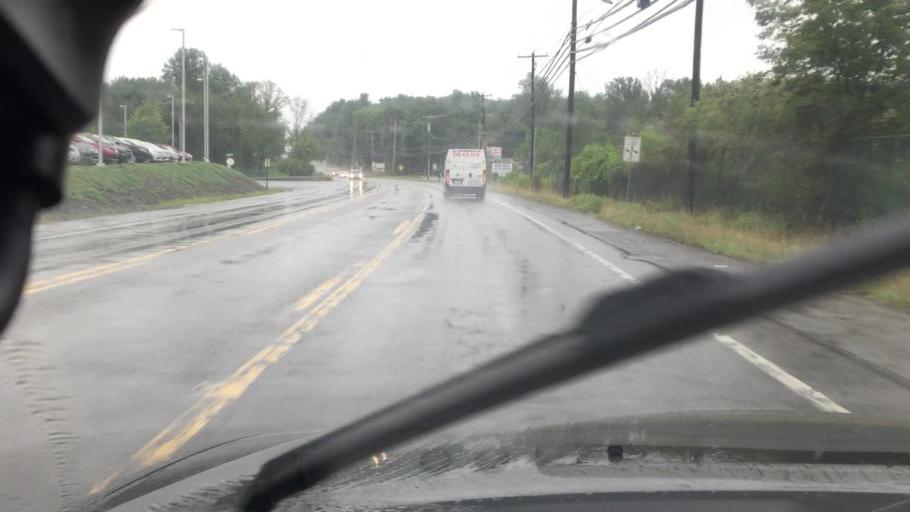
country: US
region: Pennsylvania
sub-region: Monroe County
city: Tannersville
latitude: 41.0137
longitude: -75.2937
